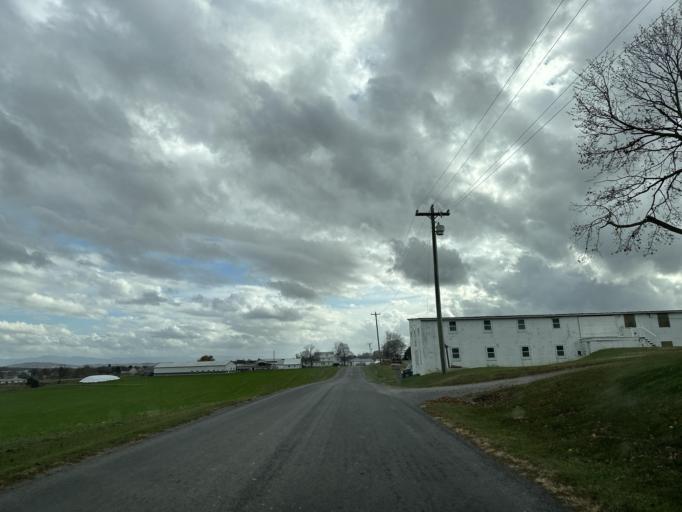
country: US
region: Virginia
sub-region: Rockingham County
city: Dayton
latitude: 38.4206
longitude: -78.9675
